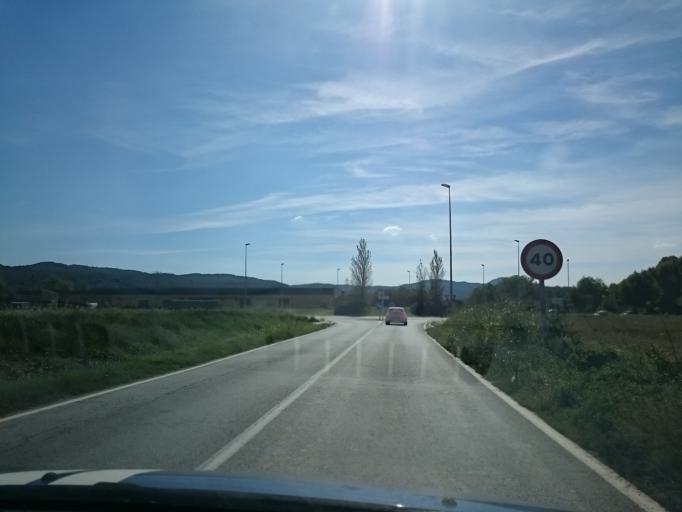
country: ES
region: Catalonia
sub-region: Provincia de Barcelona
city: Cardedeu
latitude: 41.6210
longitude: 2.3499
